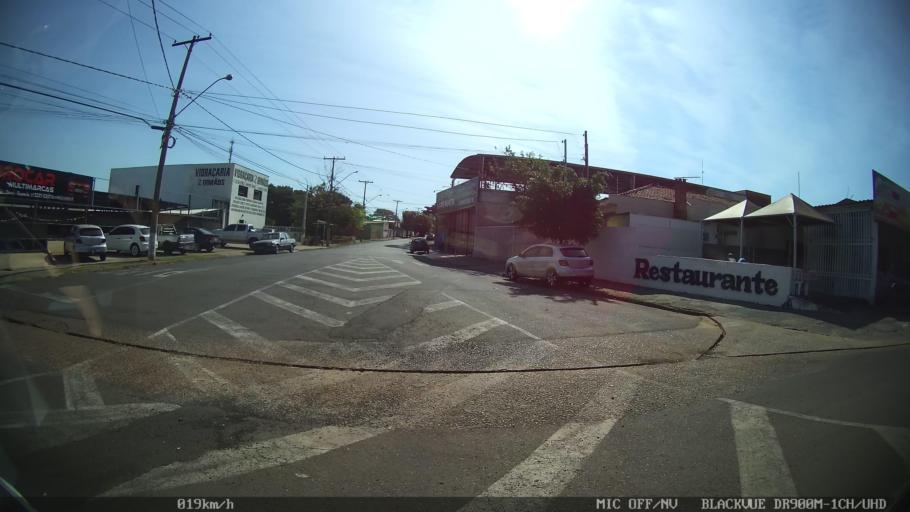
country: BR
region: Sao Paulo
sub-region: Sao Jose Do Rio Preto
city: Sao Jose do Rio Preto
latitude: -20.7914
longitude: -49.4047
